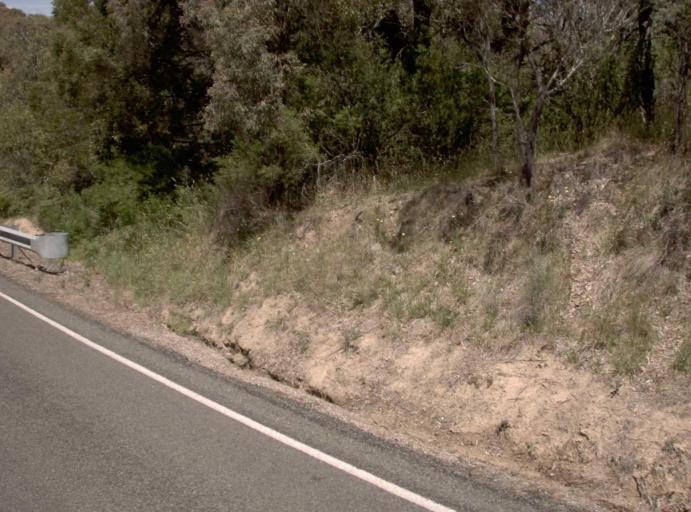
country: AU
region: Victoria
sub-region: Alpine
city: Mount Beauty
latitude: -37.1544
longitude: 147.6523
